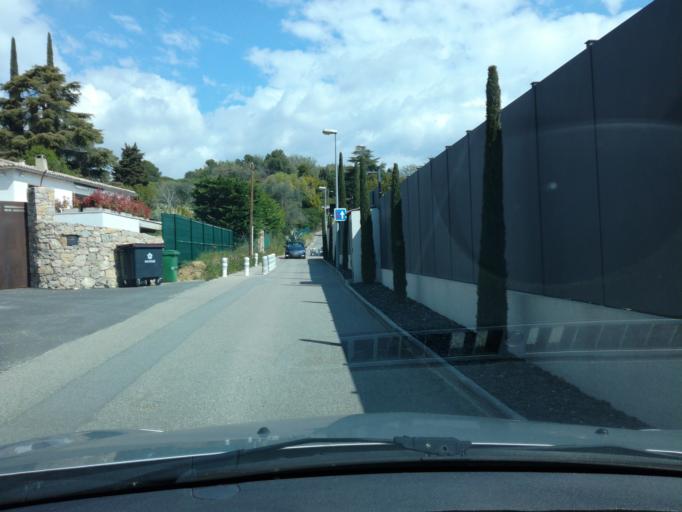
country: FR
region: Provence-Alpes-Cote d'Azur
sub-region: Departement des Alpes-Maritimes
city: Mougins
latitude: 43.6089
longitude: 6.9917
